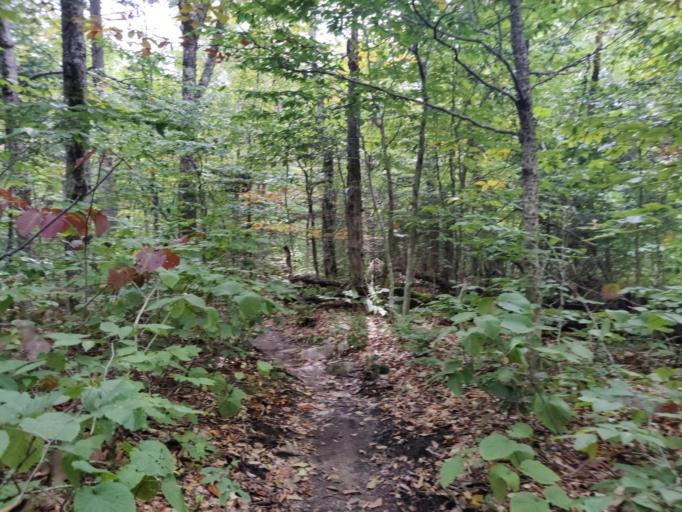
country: US
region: Vermont
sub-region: Bennington County
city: Manchester Center
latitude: 43.2588
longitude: -72.9394
